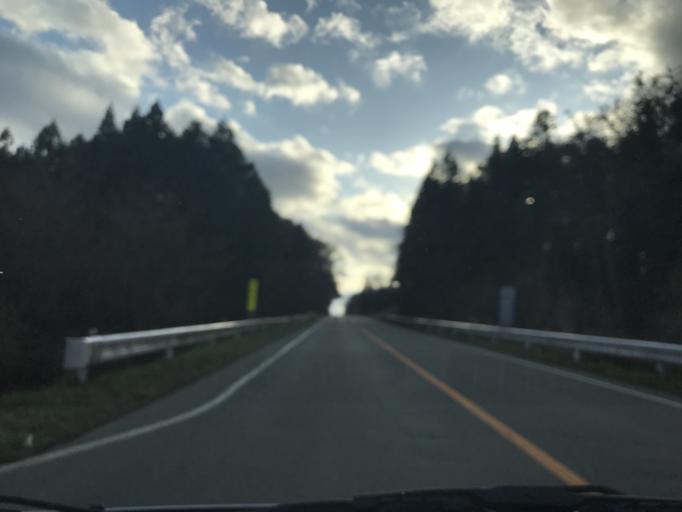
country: JP
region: Iwate
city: Mizusawa
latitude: 39.1842
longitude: 141.0527
